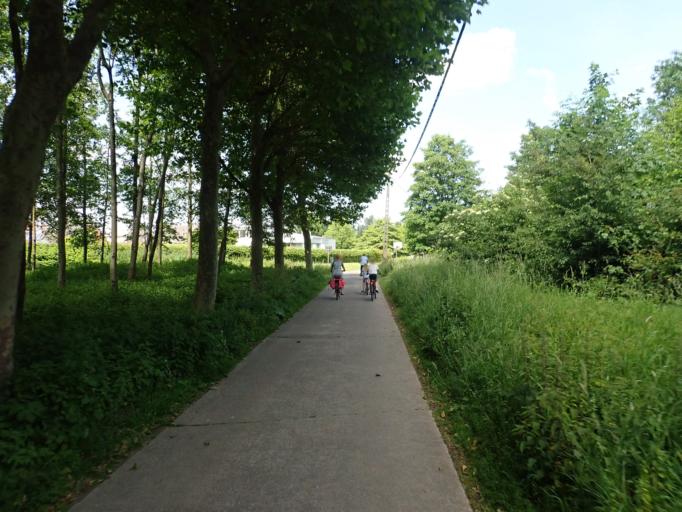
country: BE
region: Flanders
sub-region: Provincie Antwerpen
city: Willebroek
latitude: 51.0731
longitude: 4.3371
